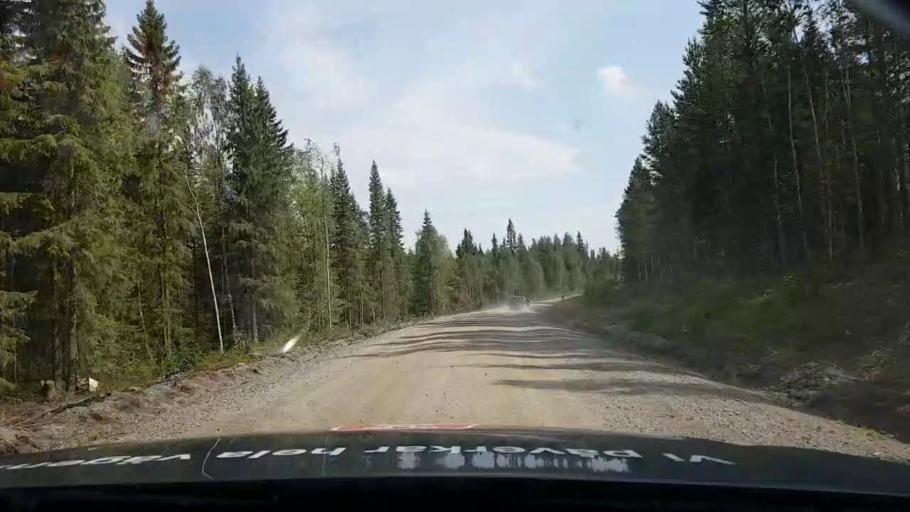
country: SE
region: Jaemtland
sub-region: Braecke Kommun
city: Braecke
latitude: 62.7388
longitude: 15.4528
